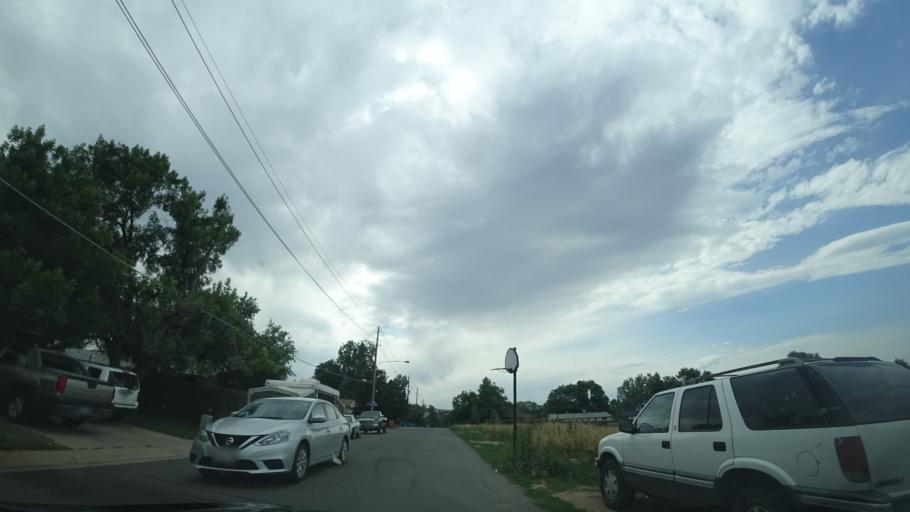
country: US
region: Colorado
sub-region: Jefferson County
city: Lakewood
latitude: 39.7094
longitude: -105.1013
